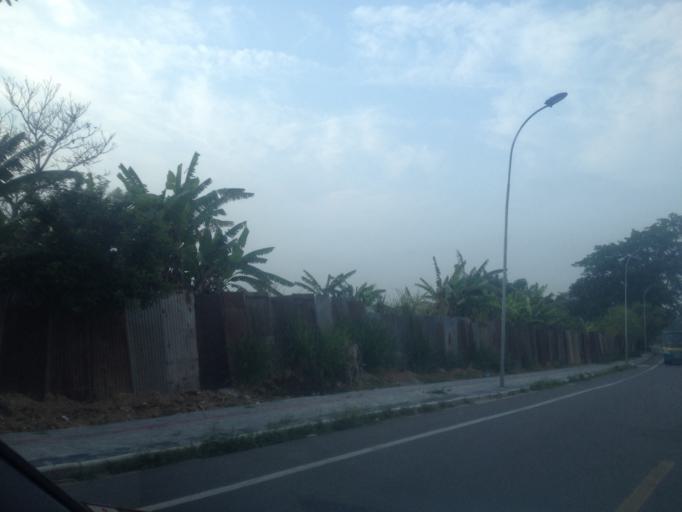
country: BR
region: Rio de Janeiro
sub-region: Porto Real
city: Porto Real
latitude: -22.4450
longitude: -44.3022
